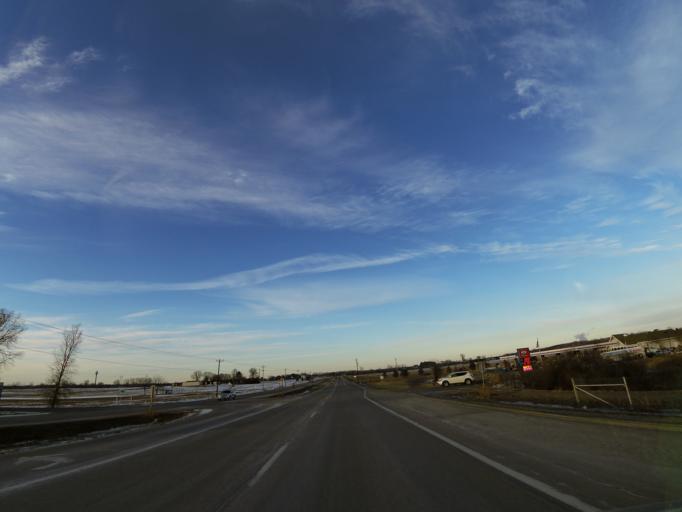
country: US
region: Minnesota
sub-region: Washington County
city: Lake Elmo
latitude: 44.9510
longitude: -92.8625
